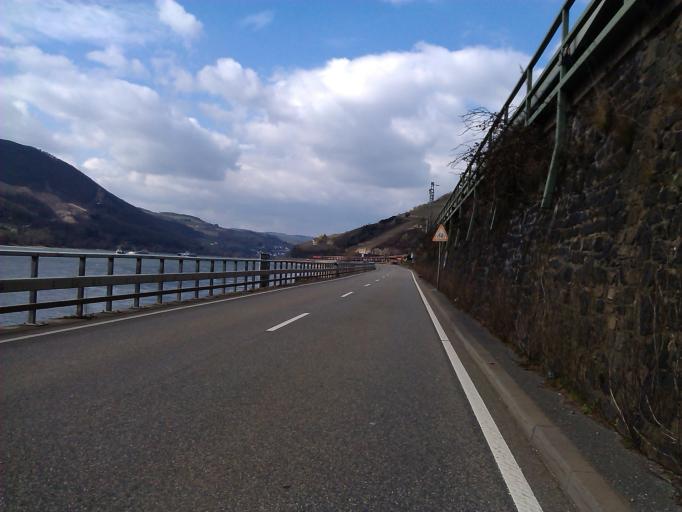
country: DE
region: Rheinland-Pfalz
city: Trechtingshausen
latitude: 50.0148
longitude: 7.8531
